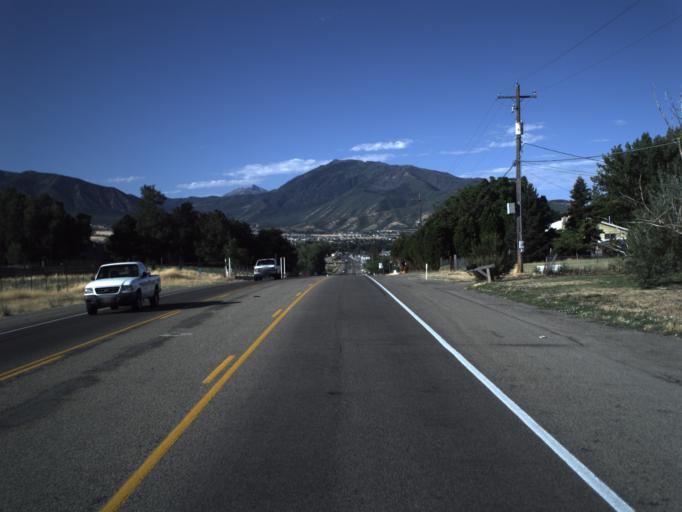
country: US
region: Utah
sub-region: Utah County
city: Salem
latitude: 40.0737
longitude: -111.6617
